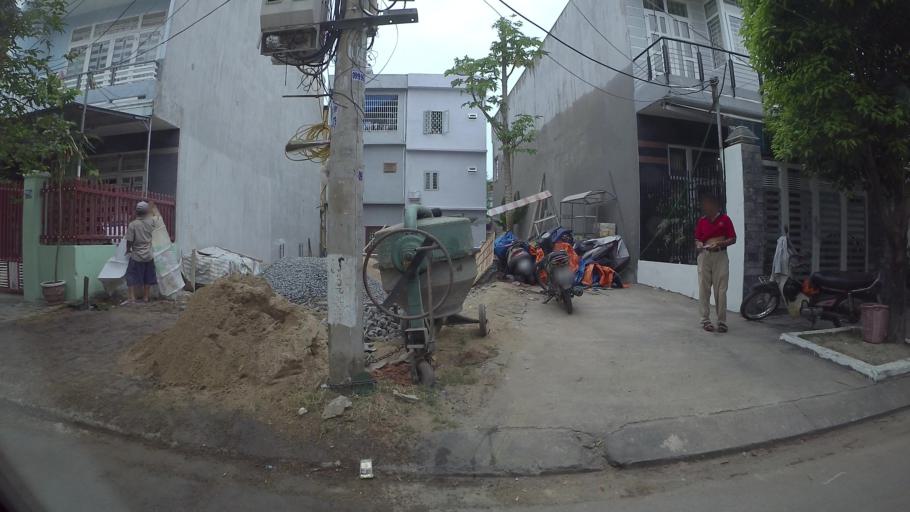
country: VN
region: Da Nang
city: Thanh Khe
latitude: 16.0587
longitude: 108.1821
